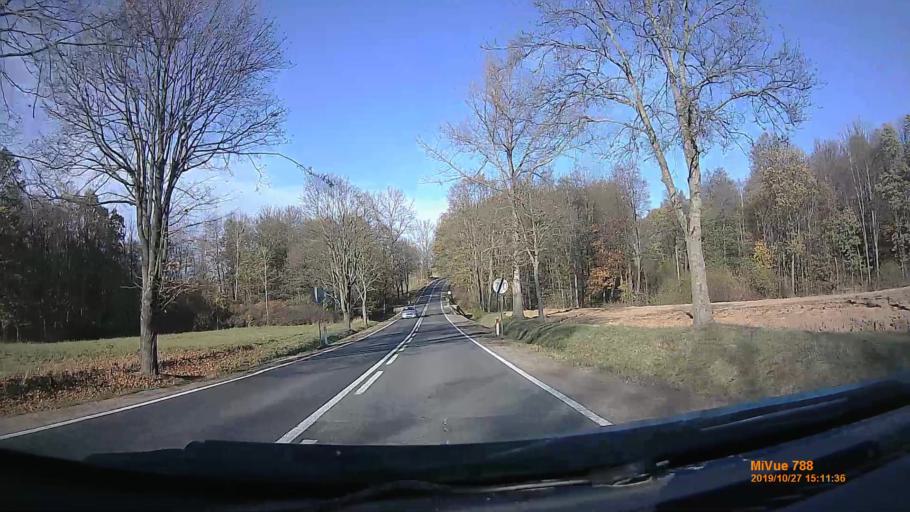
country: PL
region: Lower Silesian Voivodeship
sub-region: Powiat klodzki
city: Miedzylesie
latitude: 50.1996
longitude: 16.6722
